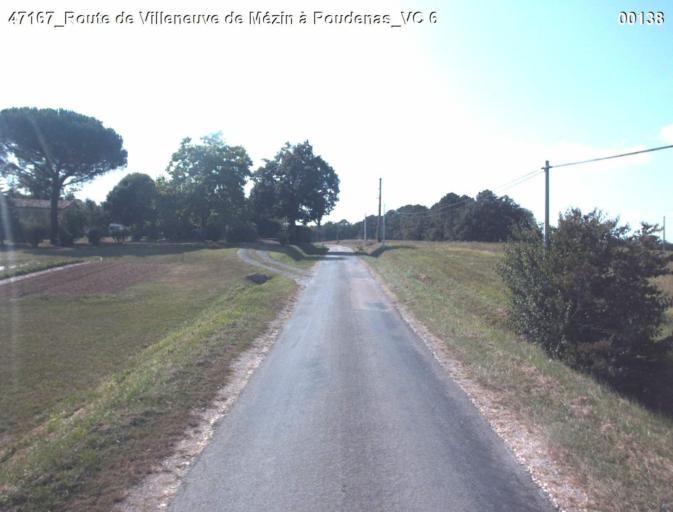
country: FR
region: Aquitaine
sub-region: Departement du Lot-et-Garonne
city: Mezin
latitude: 44.0289
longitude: 0.2342
